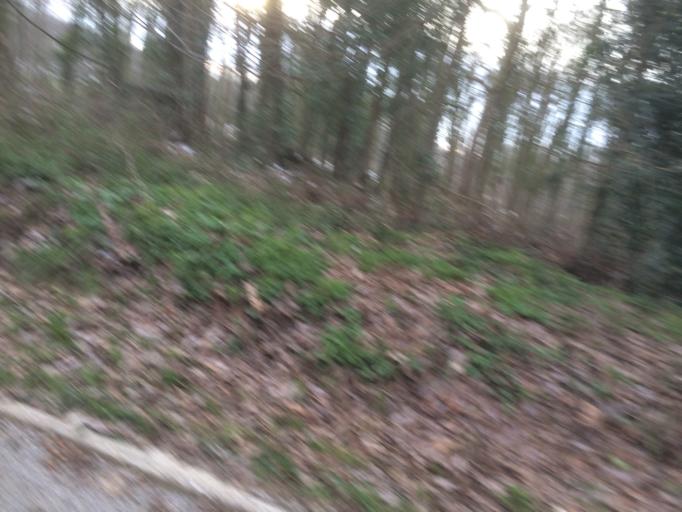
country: FR
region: Ile-de-France
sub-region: Departement de l'Essonne
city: Bures-sur-Yvette
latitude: 48.7008
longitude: 2.1765
